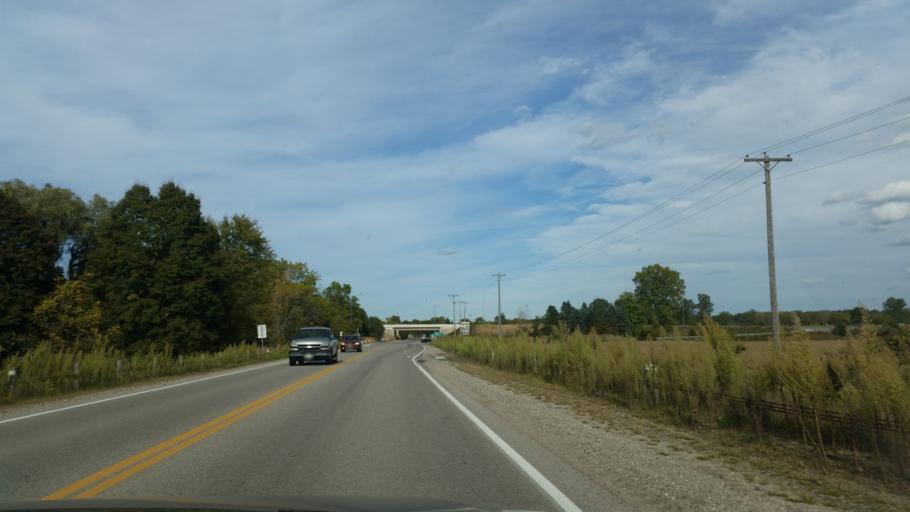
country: CA
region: Ontario
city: Delaware
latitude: 42.8977
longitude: -81.4363
